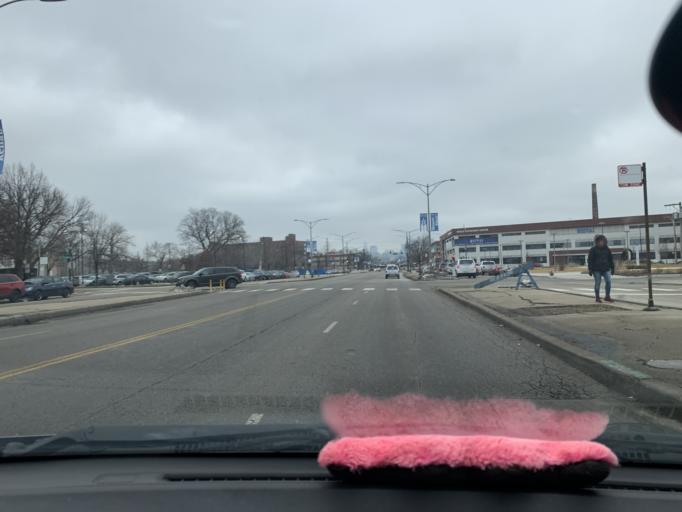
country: US
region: Illinois
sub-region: Cook County
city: Chicago
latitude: 41.8618
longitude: -87.6940
